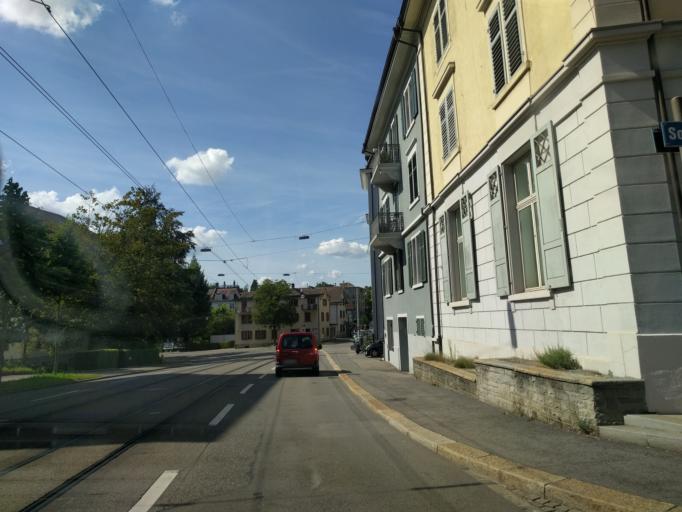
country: CH
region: Zurich
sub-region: Bezirk Zuerich
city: Zuerich (Kreis 7) / Hottingen
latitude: 47.3689
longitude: 8.5580
